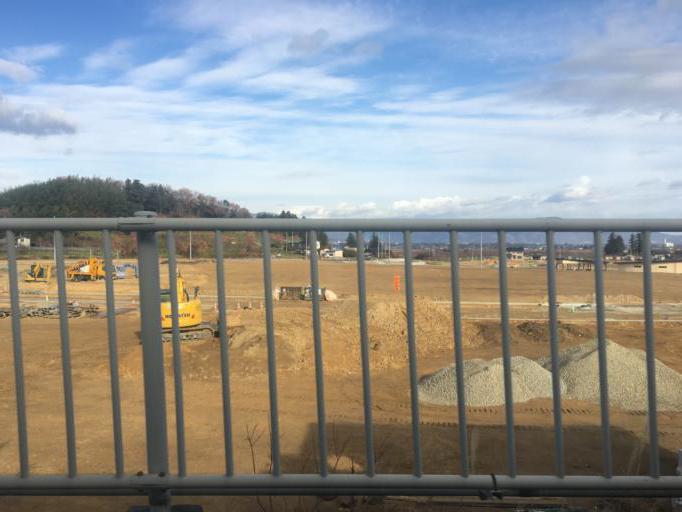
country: JP
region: Fukushima
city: Hobaramachi
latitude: 37.8087
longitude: 140.5271
